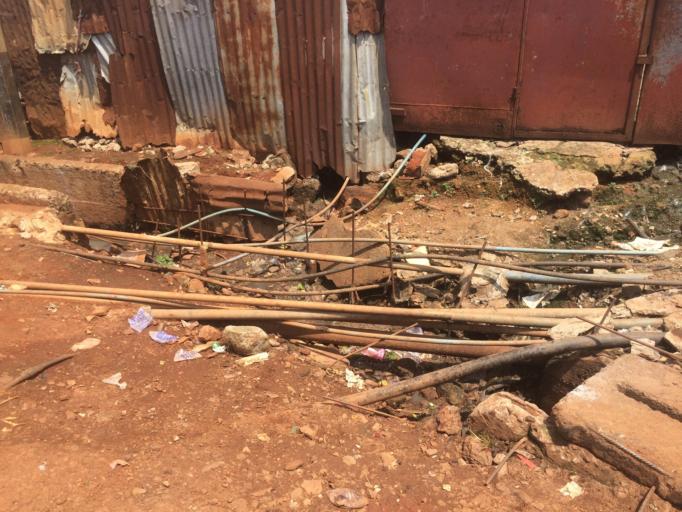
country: SL
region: Western Area
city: Freetown
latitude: 8.4786
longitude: -13.2011
